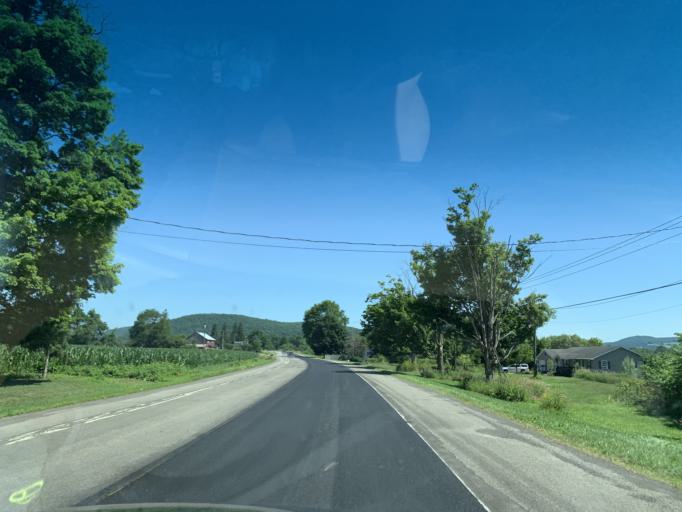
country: US
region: New York
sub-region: Delaware County
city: Sidney
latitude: 42.4095
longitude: -75.3808
